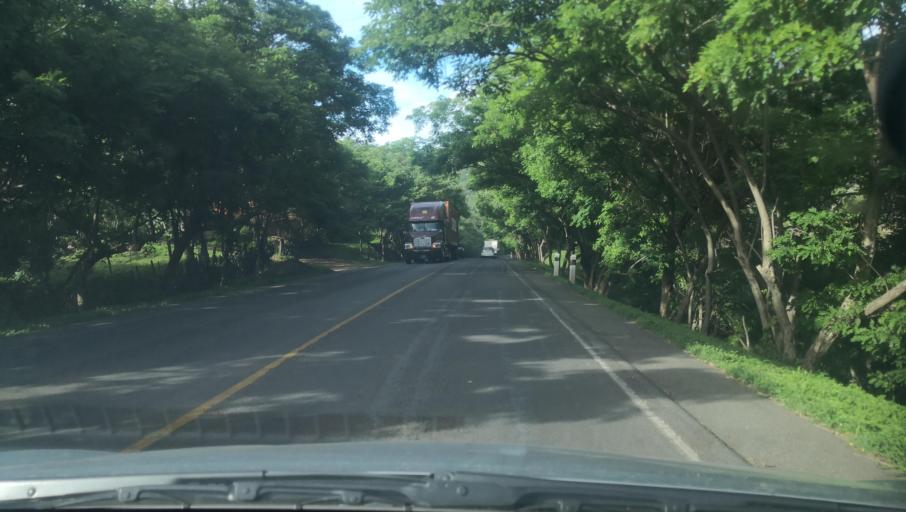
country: NI
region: Madriz
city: Totogalpa
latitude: 13.5748
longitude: -86.4807
